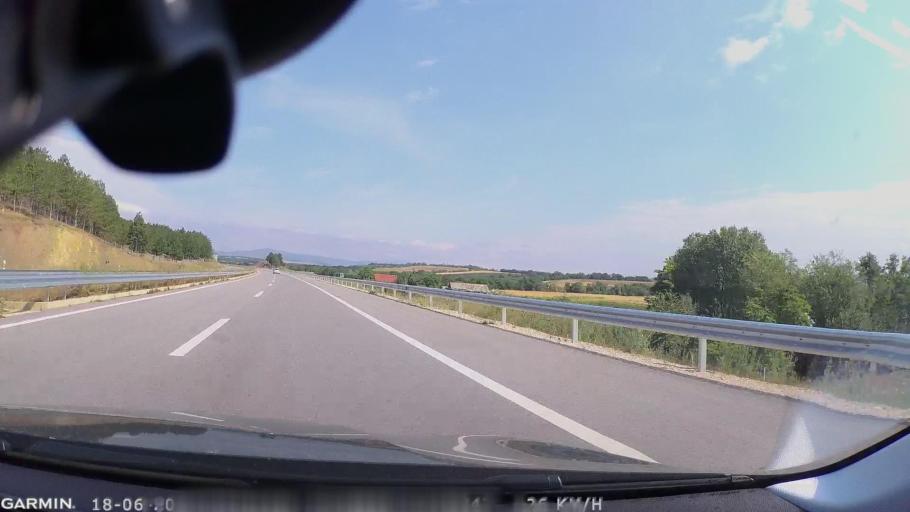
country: MK
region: Sveti Nikole
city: Sveti Nikole
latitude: 41.8860
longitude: 21.9329
